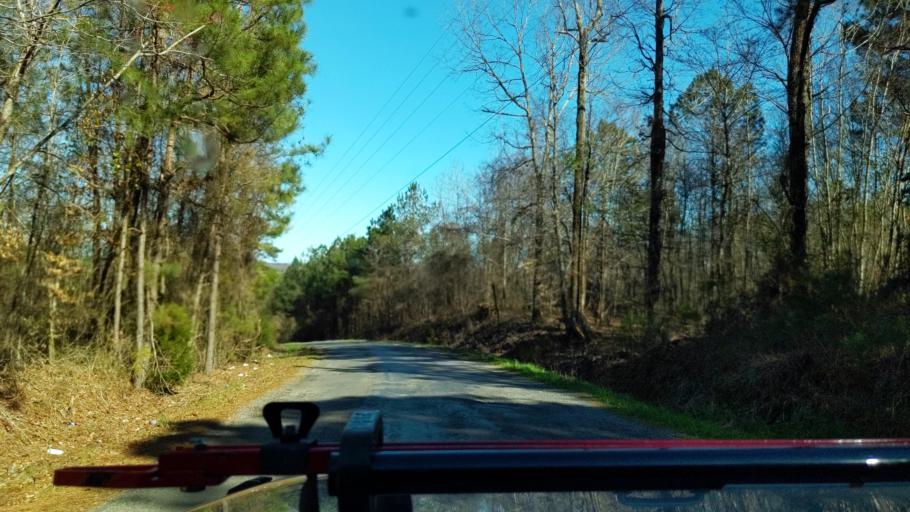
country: US
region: Alabama
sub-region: Walker County
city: Jasper
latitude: 34.0508
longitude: -87.1569
